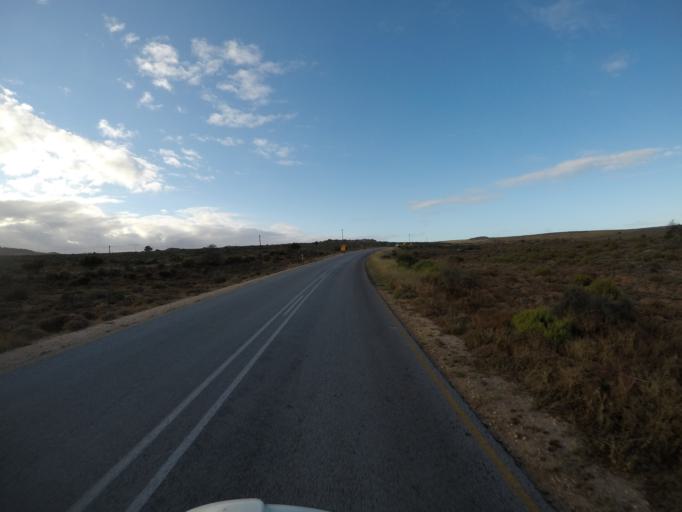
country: ZA
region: Western Cape
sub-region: West Coast District Municipality
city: Clanwilliam
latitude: -32.3329
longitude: 18.3725
